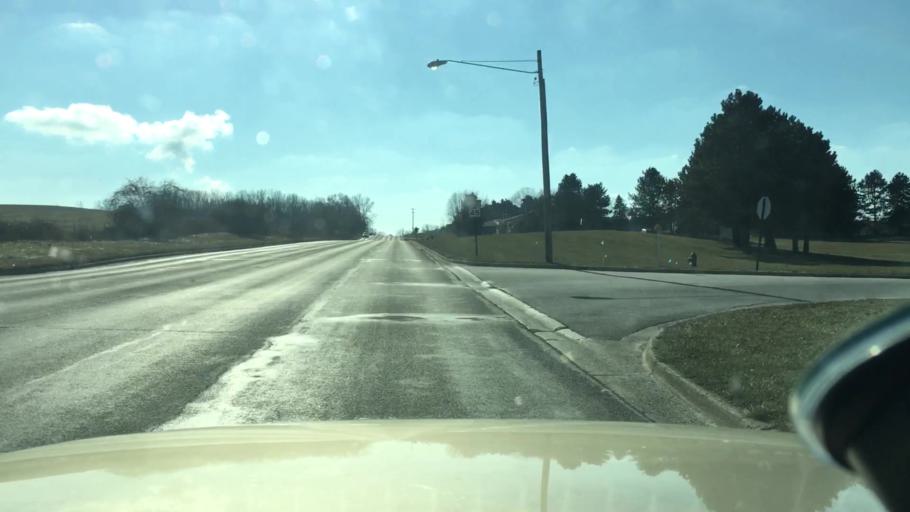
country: US
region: Michigan
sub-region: Jackson County
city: Jackson
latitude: 42.2877
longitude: -84.3844
